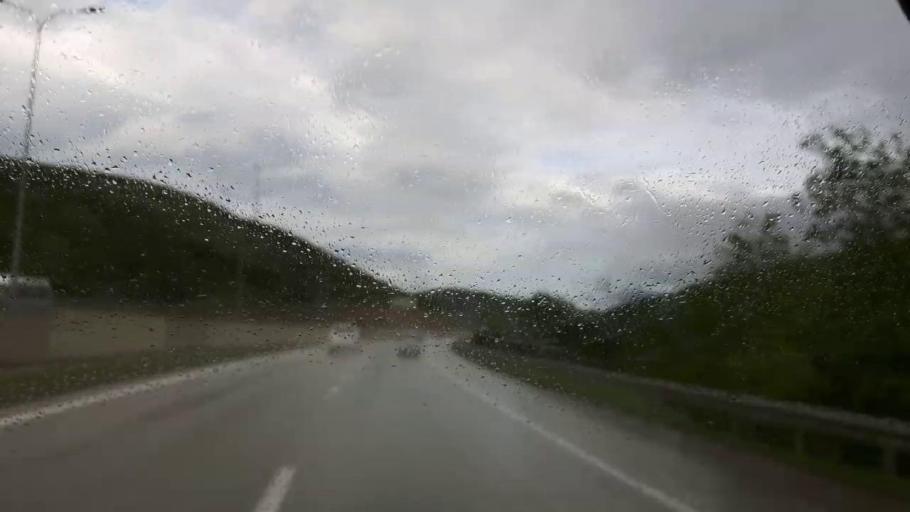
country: GE
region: Shida Kartli
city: Kaspi
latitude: 41.9962
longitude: 44.4051
